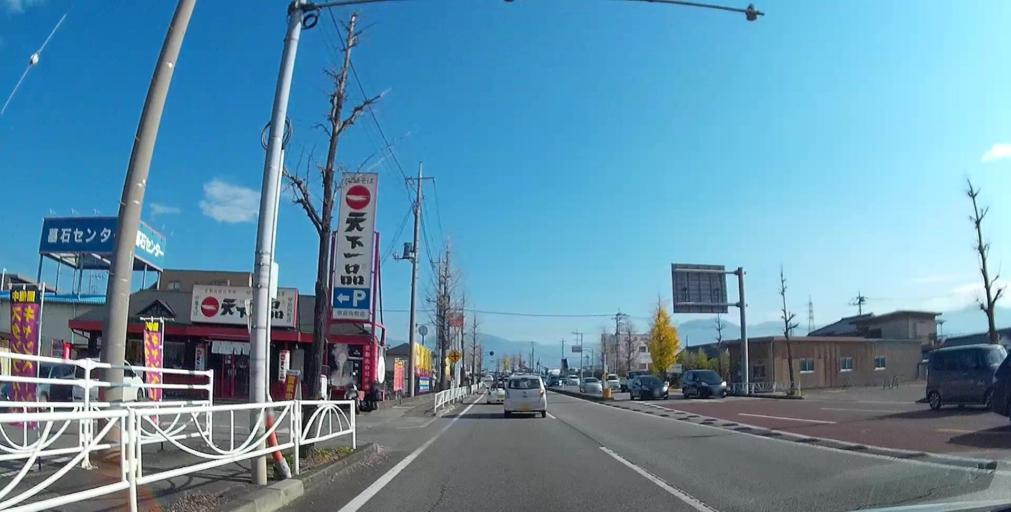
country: JP
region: Yamanashi
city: Isawa
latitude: 35.6454
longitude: 138.6157
